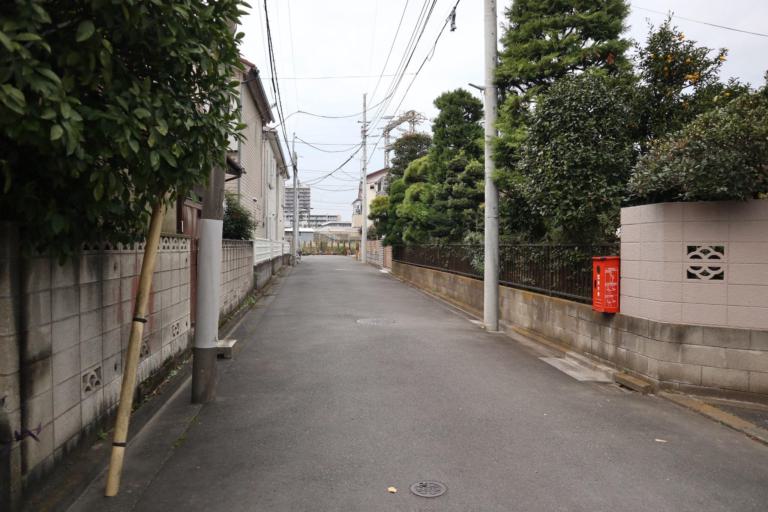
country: JP
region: Chiba
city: Matsudo
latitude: 35.7460
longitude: 139.8652
